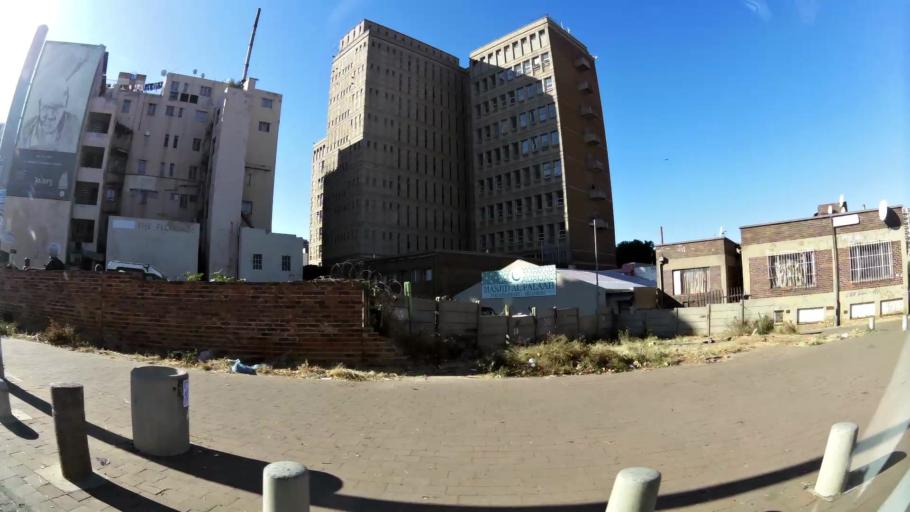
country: ZA
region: Gauteng
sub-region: City of Johannesburg Metropolitan Municipality
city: Johannesburg
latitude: -26.1906
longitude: 28.0437
